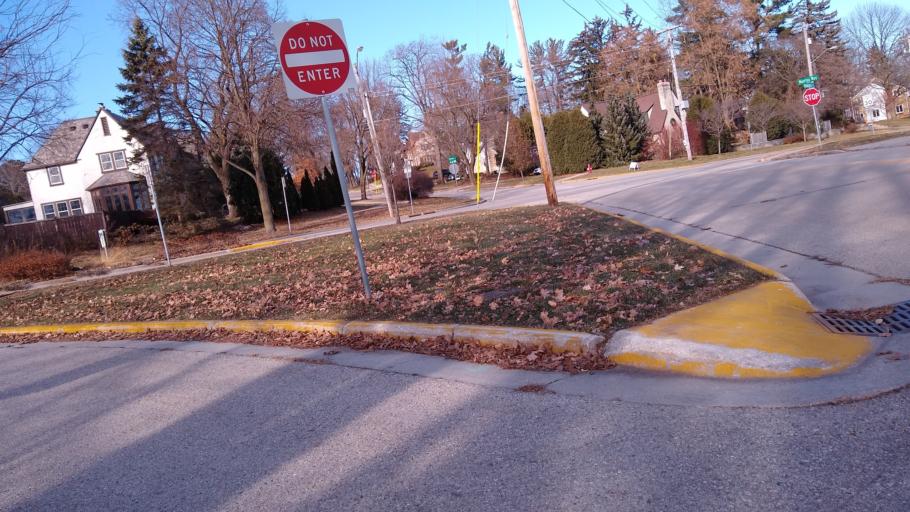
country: US
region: Wisconsin
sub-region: Dane County
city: Shorewood Hills
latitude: 43.0480
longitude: -89.4387
